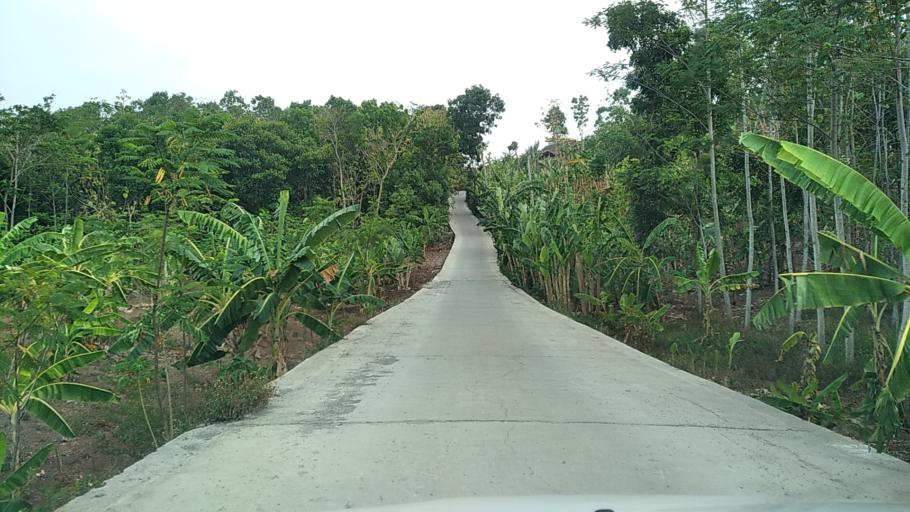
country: ID
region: Central Java
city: Semarang
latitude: -6.9975
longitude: 110.3072
